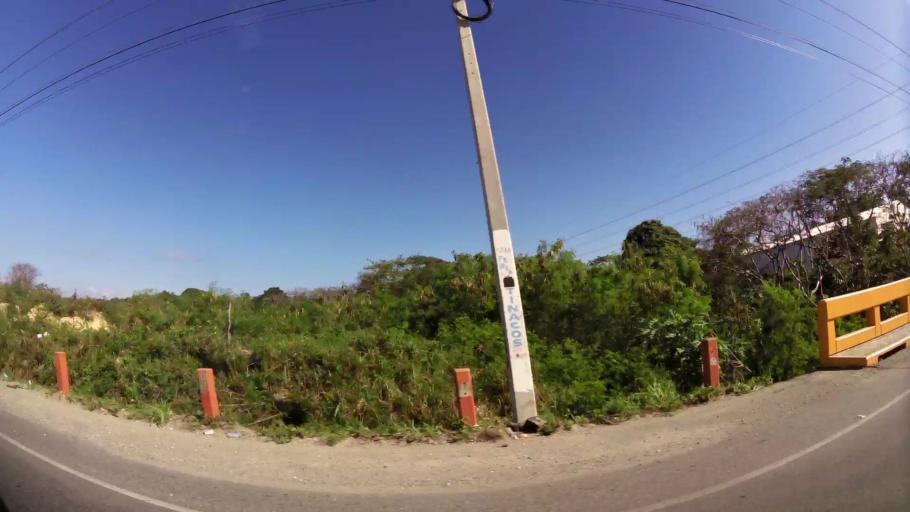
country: DO
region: San Cristobal
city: Bajos de Haina
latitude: 18.4312
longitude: -70.0551
